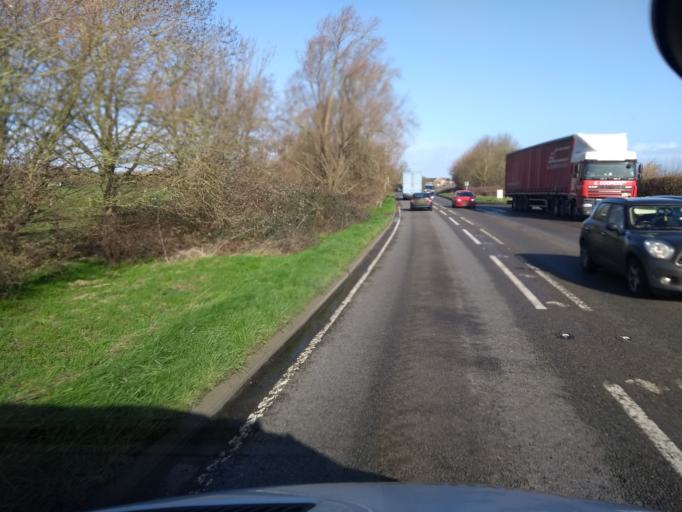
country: GB
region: England
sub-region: Somerset
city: Ilchester
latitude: 50.9967
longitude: -2.6807
